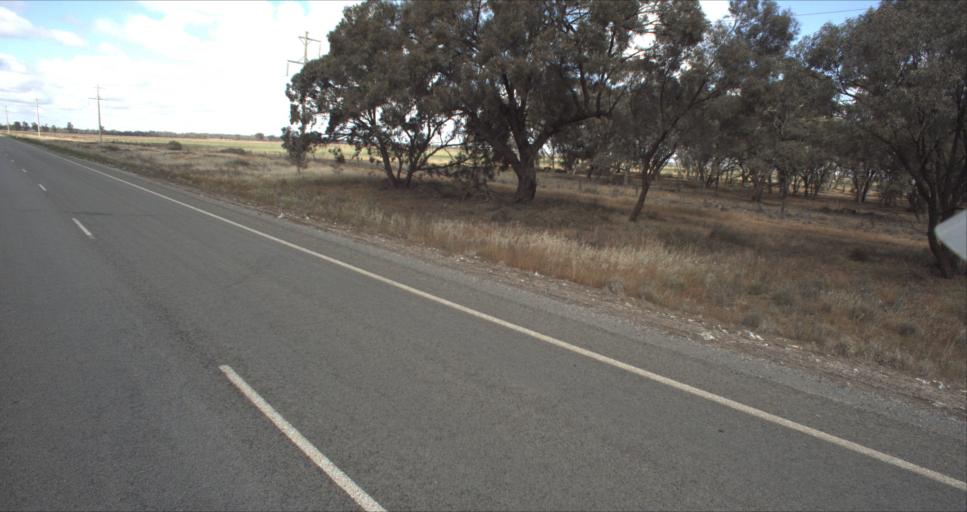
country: AU
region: New South Wales
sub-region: Murrumbidgee Shire
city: Darlington Point
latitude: -34.5764
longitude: 146.1660
